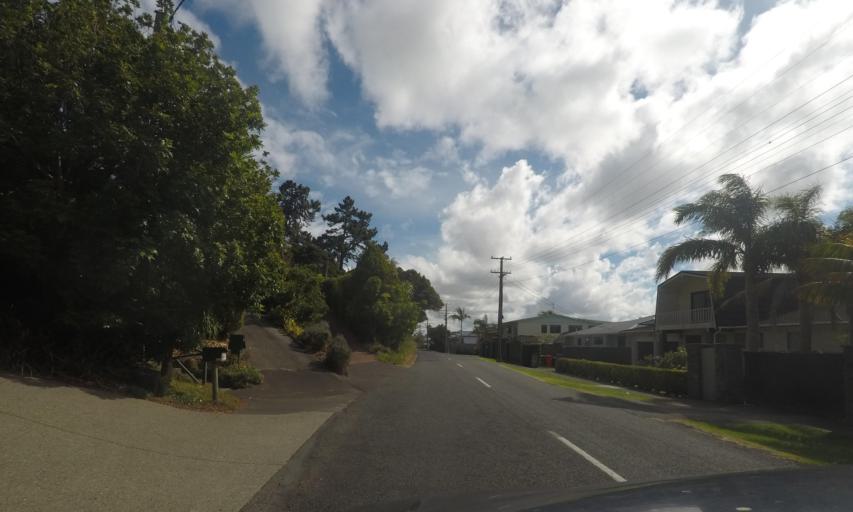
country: NZ
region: Auckland
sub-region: Auckland
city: North Shore
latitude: -36.7785
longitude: 174.6562
